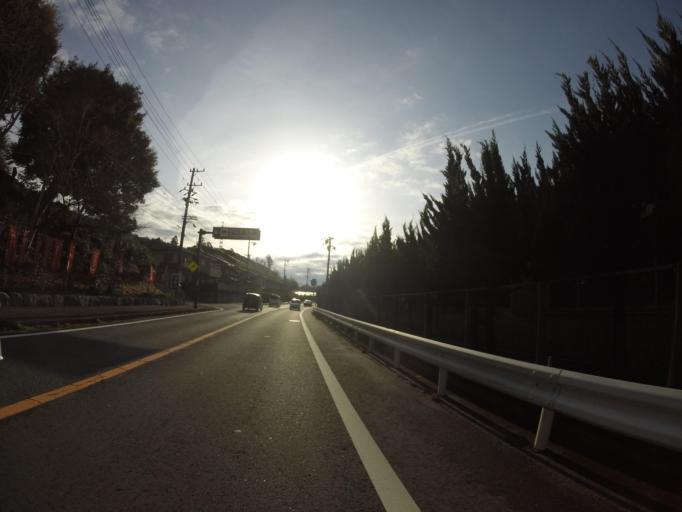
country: JP
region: Shizuoka
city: Hamakita
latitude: 34.8162
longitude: 137.6916
